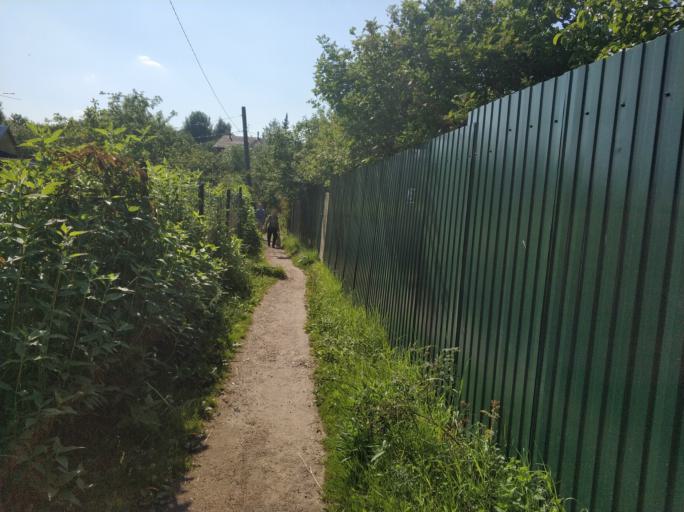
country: RU
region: St.-Petersburg
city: Gorelovo
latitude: 59.7507
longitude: 30.1164
